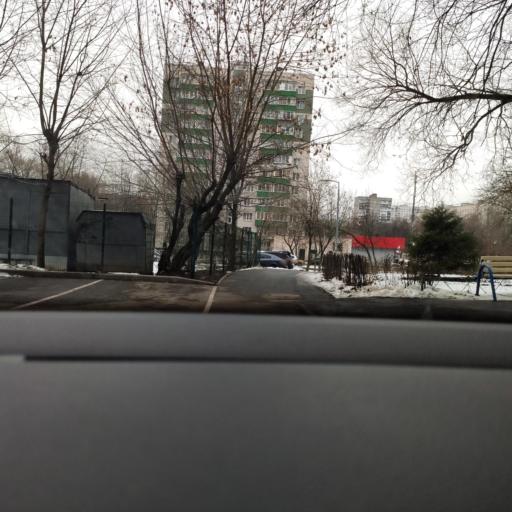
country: RU
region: Moscow
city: Gol'yanovo
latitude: 55.8180
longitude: 37.8188
